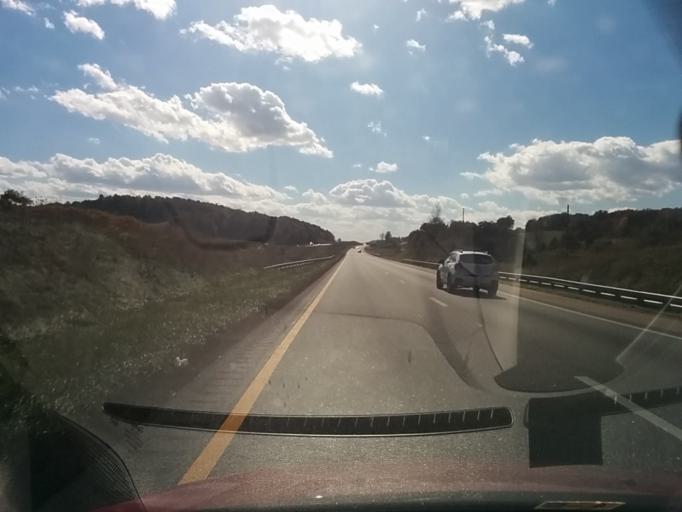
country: US
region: Virginia
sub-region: Augusta County
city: Stuarts Draft
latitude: 37.9430
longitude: -79.2181
